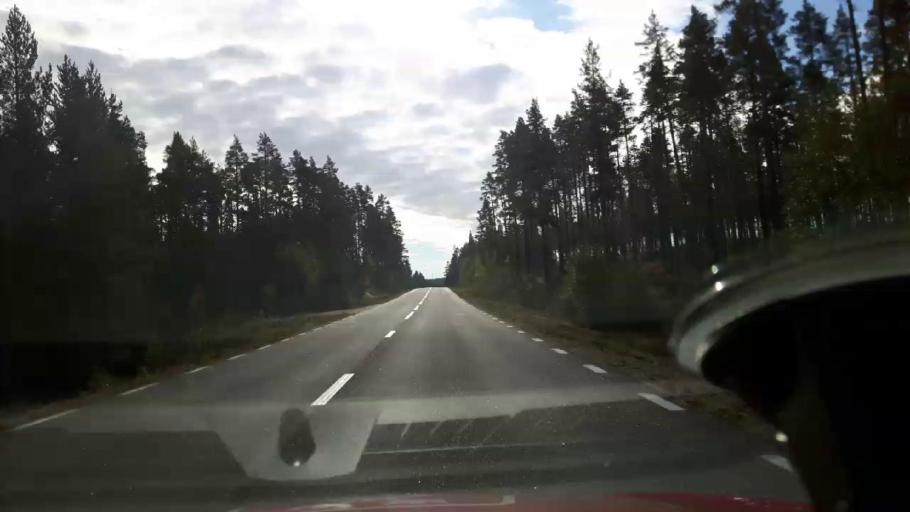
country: SE
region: Gaevleborg
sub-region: Ljusdals Kommun
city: Farila
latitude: 62.0232
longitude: 15.2277
